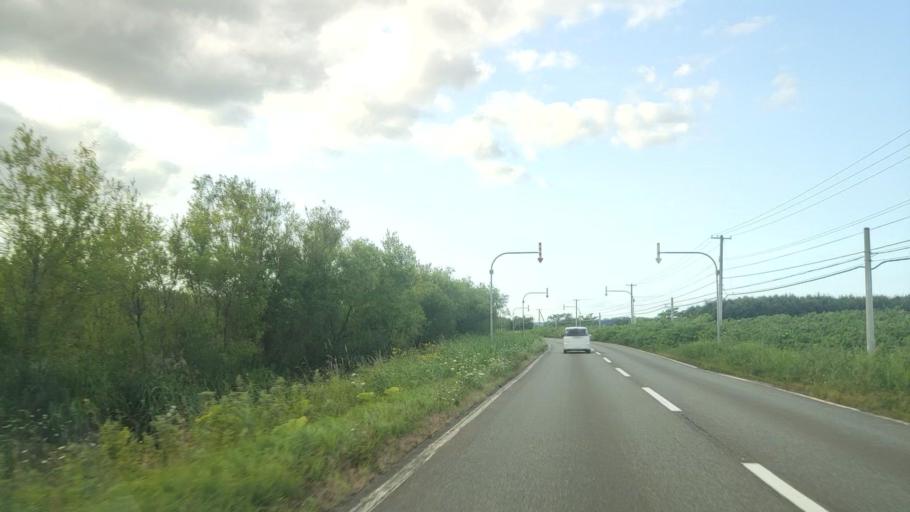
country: JP
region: Hokkaido
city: Makubetsu
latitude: 44.9988
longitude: 141.8167
